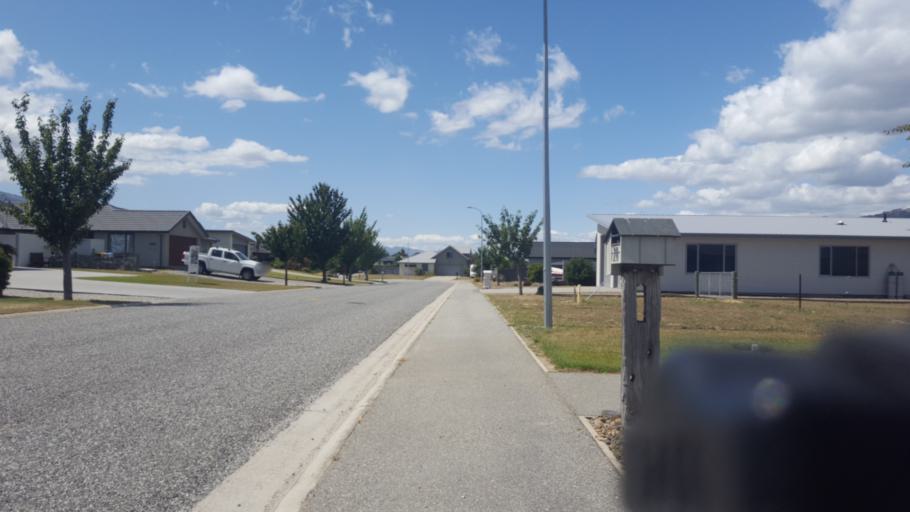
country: NZ
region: Otago
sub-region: Queenstown-Lakes District
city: Wanaka
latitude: -44.9721
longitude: 169.2485
